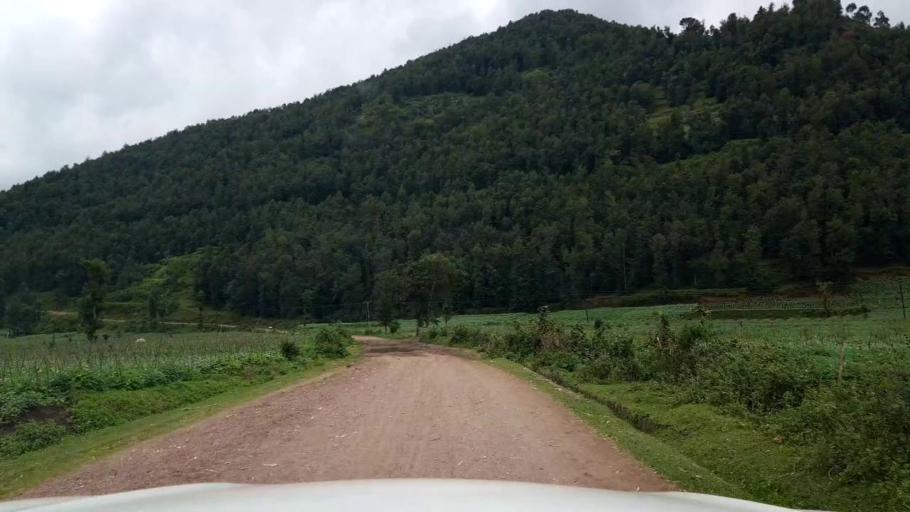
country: RW
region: Western Province
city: Gisenyi
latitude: -1.6462
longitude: 29.4104
